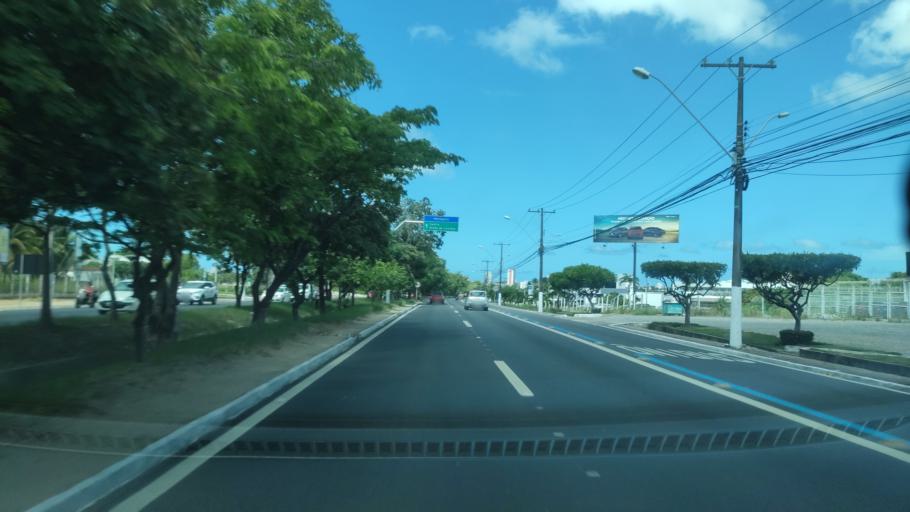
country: BR
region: Alagoas
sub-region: Maceio
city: Maceio
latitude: -9.6039
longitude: -35.7449
